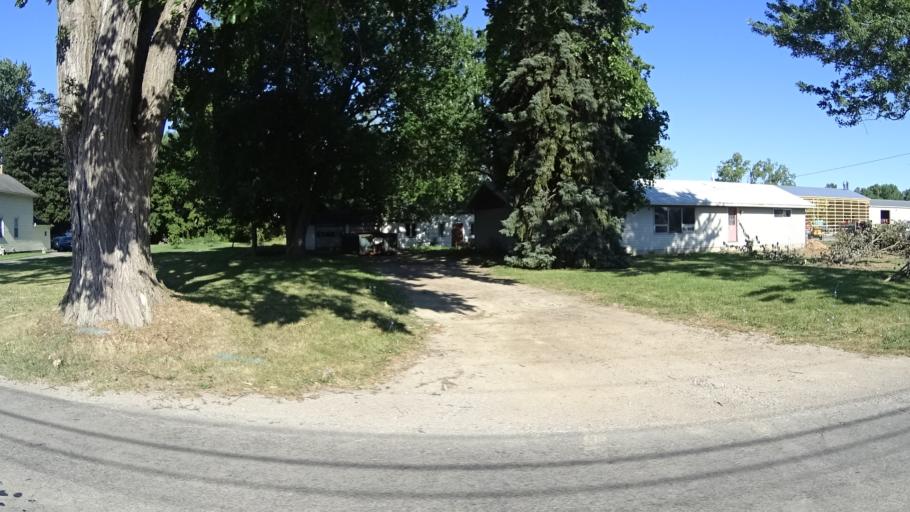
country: US
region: Ohio
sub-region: Erie County
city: Sandusky
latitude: 41.4229
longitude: -82.7349
